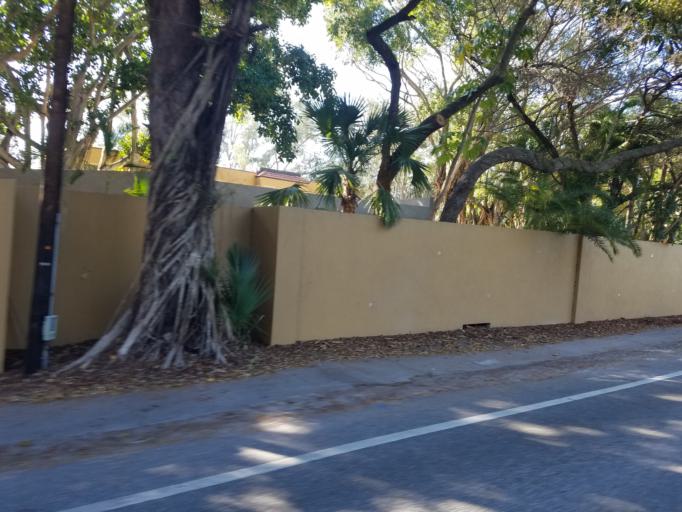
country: US
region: Florida
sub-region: Sarasota County
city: Gulf Gate Estates
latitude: 27.2322
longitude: -82.5212
